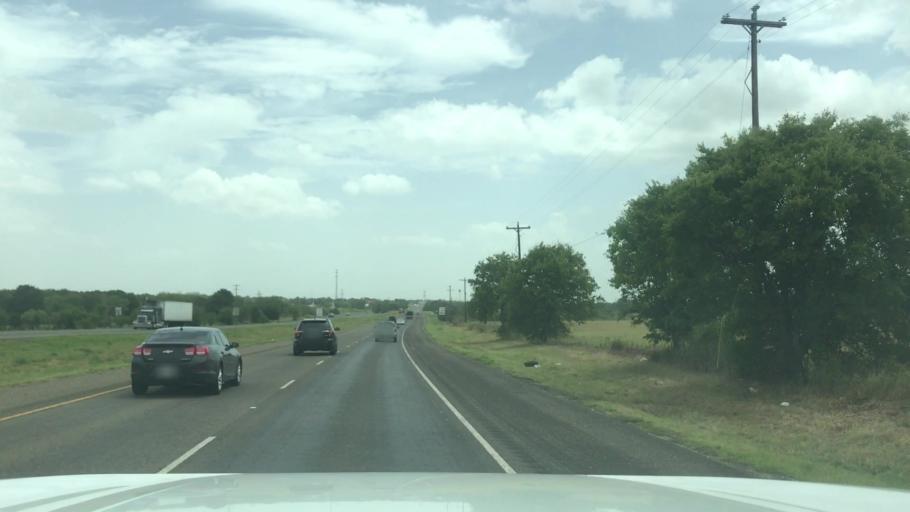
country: US
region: Texas
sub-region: McLennan County
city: Riesel
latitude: 31.4870
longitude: -96.9276
